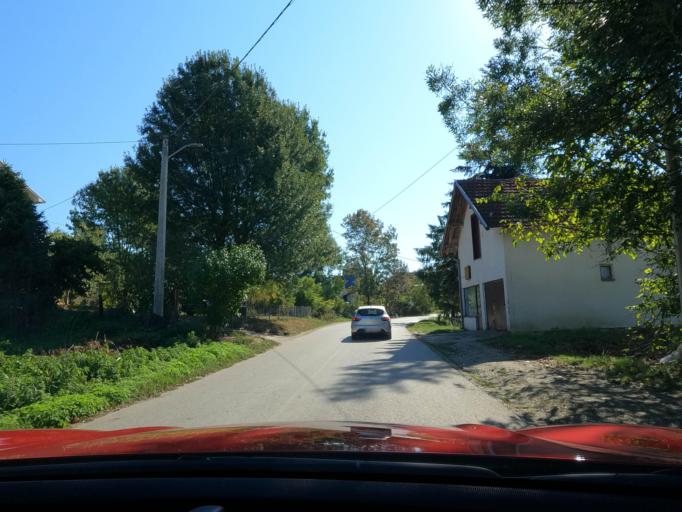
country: RS
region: Central Serbia
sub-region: Raski Okrug
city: Kraljevo
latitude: 43.7639
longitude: 20.6740
